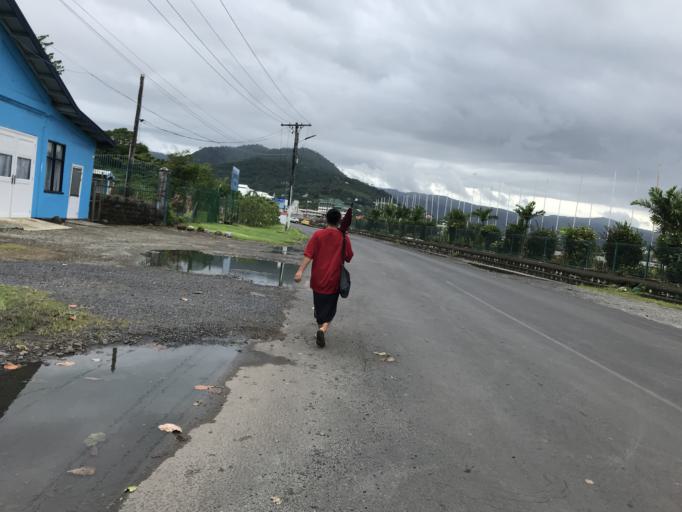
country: WS
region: Tuamasaga
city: Apia
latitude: -13.8285
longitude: -171.7590
